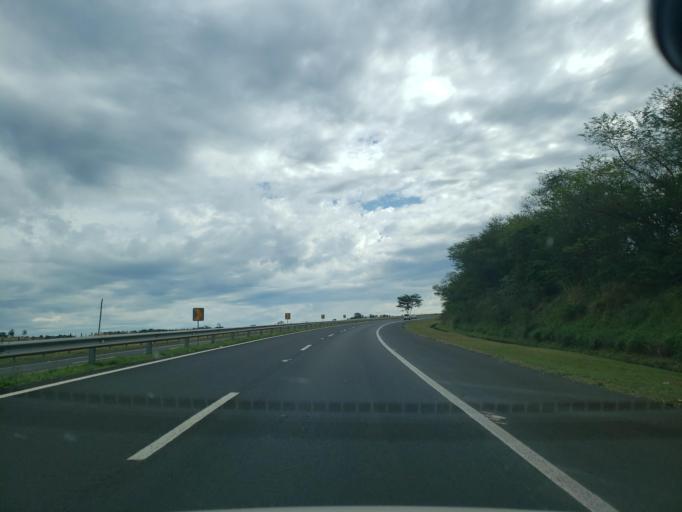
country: BR
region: Sao Paulo
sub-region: Bauru
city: Bauru
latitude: -22.1962
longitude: -49.1973
